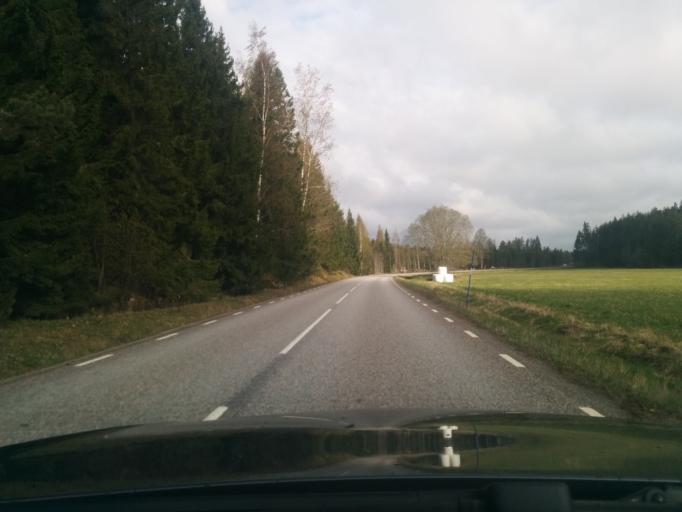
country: SE
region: Uppsala
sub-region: Tierps Kommun
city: Orbyhus
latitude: 60.2042
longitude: 17.7001
